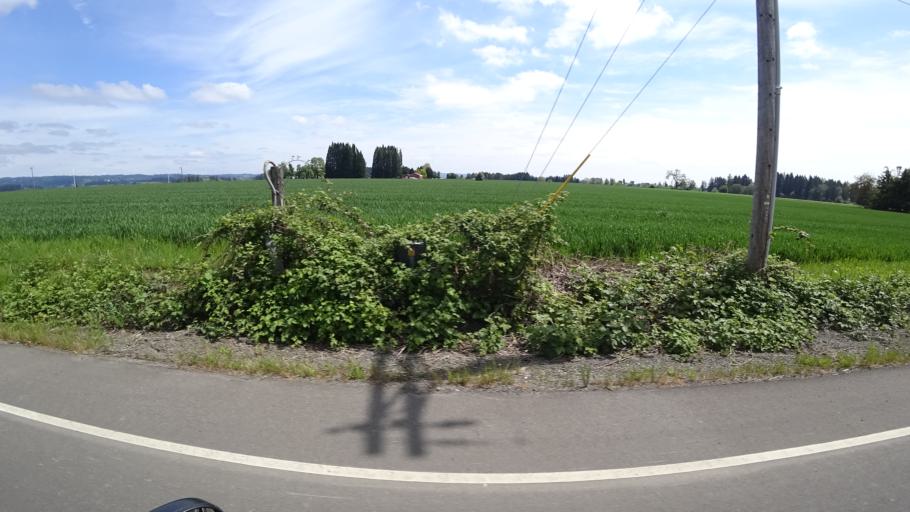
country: US
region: Oregon
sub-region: Washington County
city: North Plains
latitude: 45.5706
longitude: -122.9704
